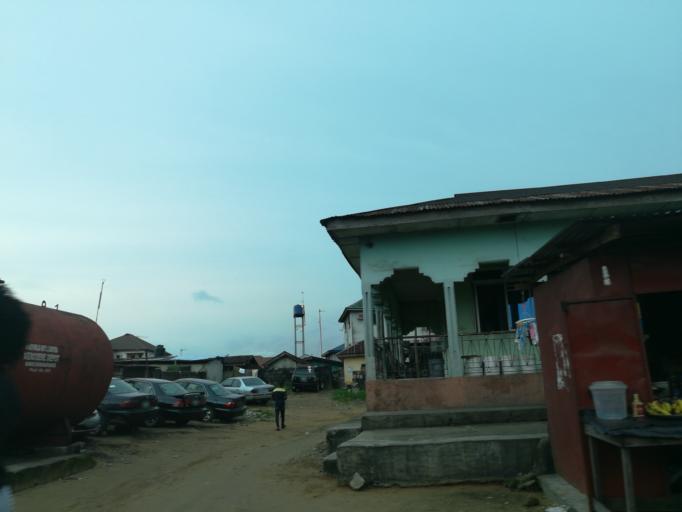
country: NG
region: Rivers
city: Port Harcourt
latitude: 4.8138
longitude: 7.0223
